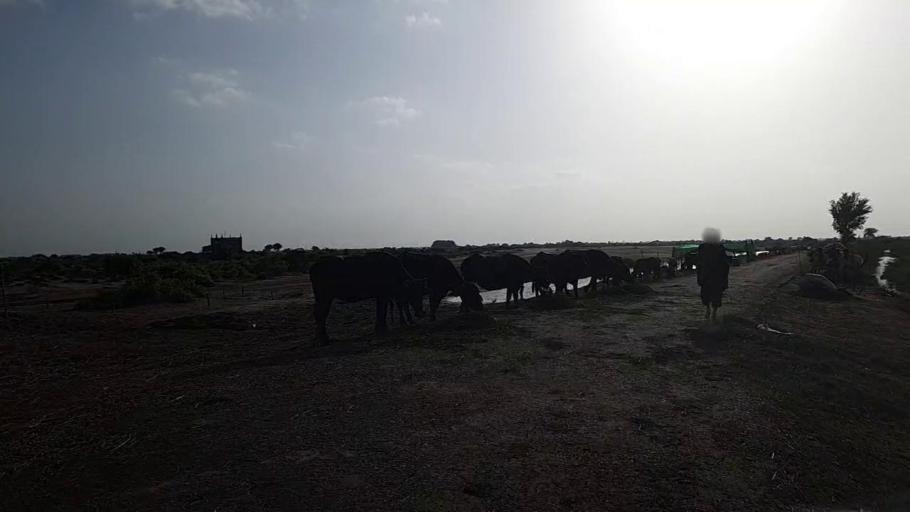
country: PK
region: Sindh
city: Mirpur Batoro
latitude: 24.6681
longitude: 68.4543
